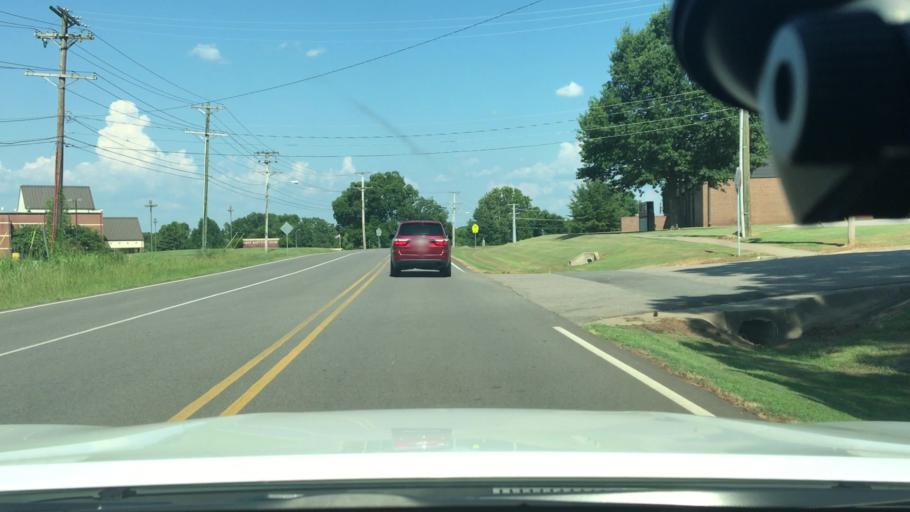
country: US
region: Arkansas
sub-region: Johnson County
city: Clarksville
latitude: 35.4617
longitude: -93.4838
